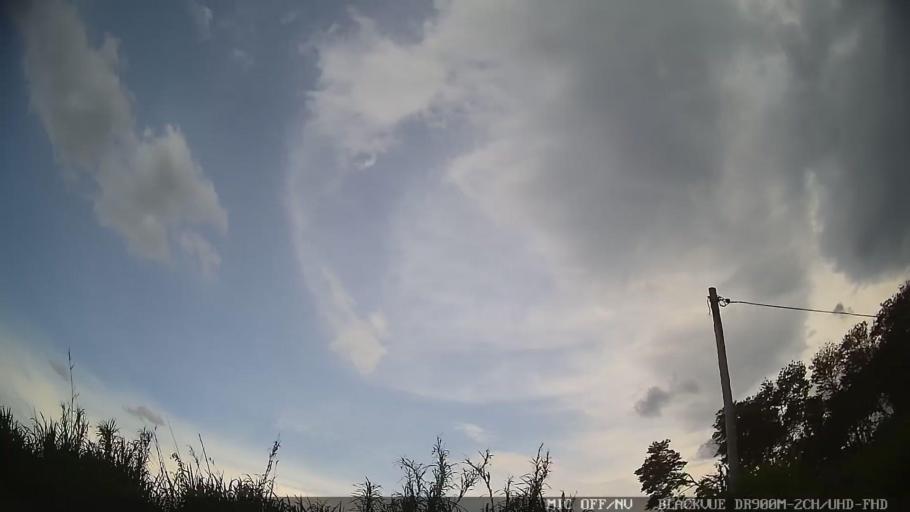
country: BR
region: Sao Paulo
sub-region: Itatiba
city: Itatiba
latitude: -22.9335
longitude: -46.7915
